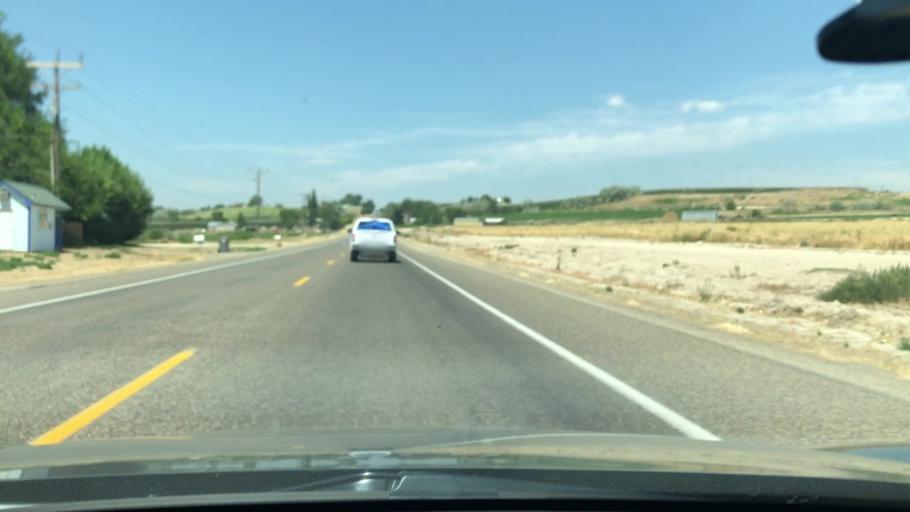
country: US
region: Idaho
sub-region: Canyon County
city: Wilder
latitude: 43.6502
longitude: -116.9116
